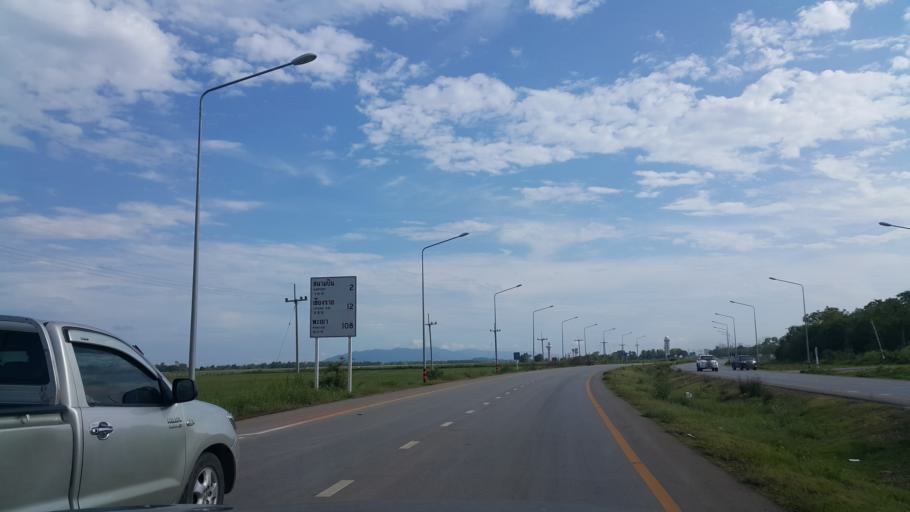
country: TH
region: Chiang Rai
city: Chiang Rai
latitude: 19.9713
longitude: 99.8876
